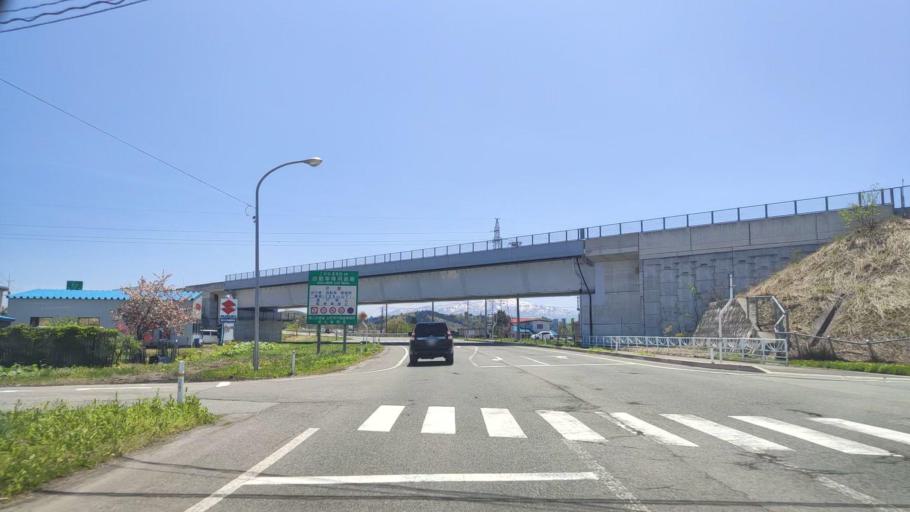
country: JP
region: Yamagata
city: Shinjo
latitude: 38.7452
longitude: 140.2948
